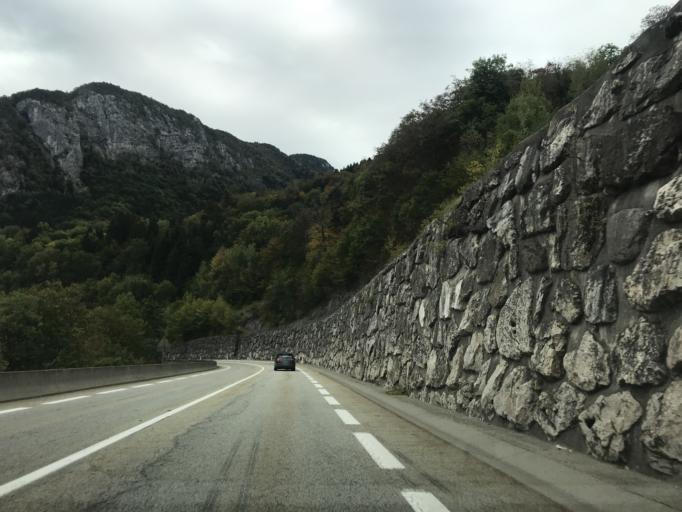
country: FR
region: Rhone-Alpes
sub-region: Departement de la Haute-Savoie
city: Dingy-Saint-Clair
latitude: 45.9098
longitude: 6.1983
